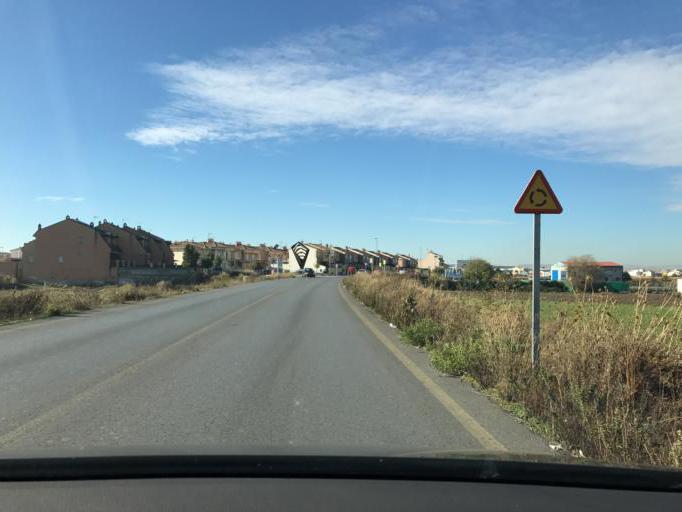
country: ES
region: Andalusia
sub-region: Provincia de Granada
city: Armilla
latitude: 37.1509
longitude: -3.6251
